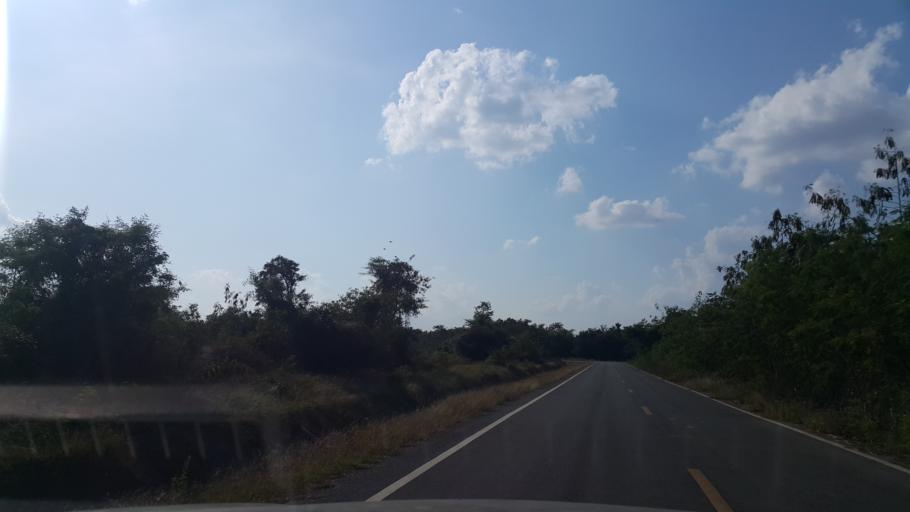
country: TH
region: Lamphun
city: Mae Tha
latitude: 18.5222
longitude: 99.0970
